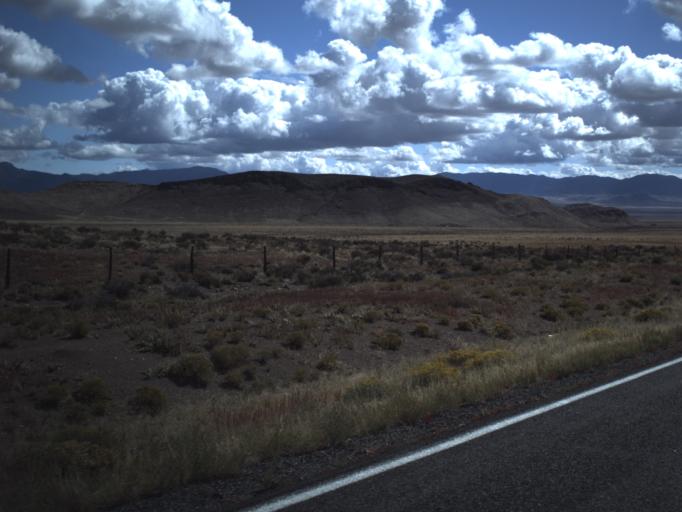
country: US
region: Utah
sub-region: Beaver County
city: Milford
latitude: 38.6045
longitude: -113.8345
